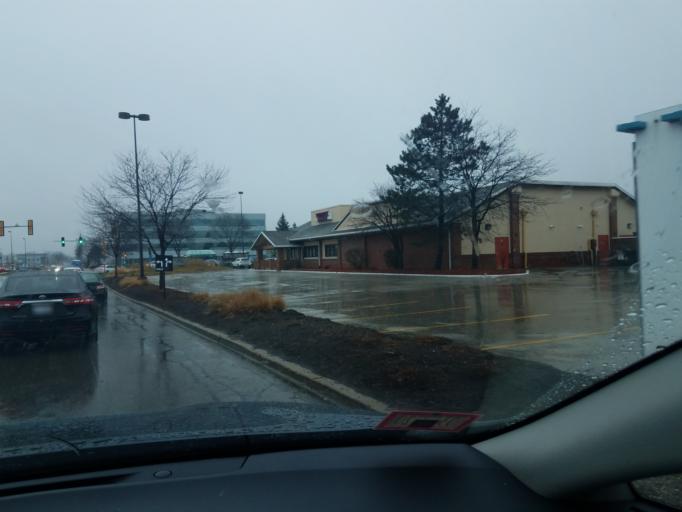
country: US
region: Illinois
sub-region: Cook County
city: Morton Grove
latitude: 42.0110
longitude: -87.7674
